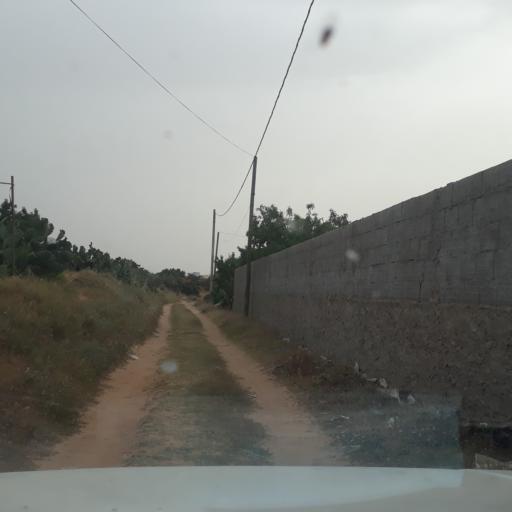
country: TN
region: Safaqis
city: Al Qarmadah
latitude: 34.8219
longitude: 10.7716
